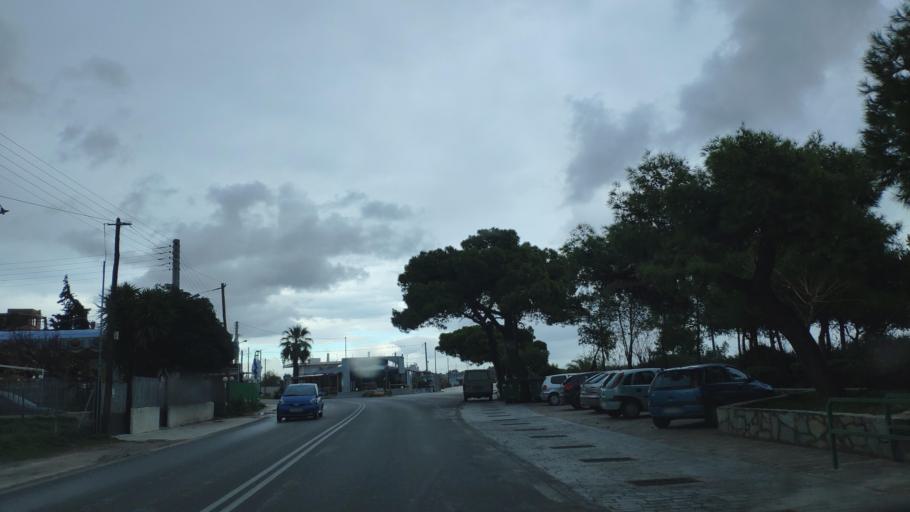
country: GR
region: Attica
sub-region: Nomarchia Anatolikis Attikis
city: Artemida
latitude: 37.9847
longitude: 24.0120
